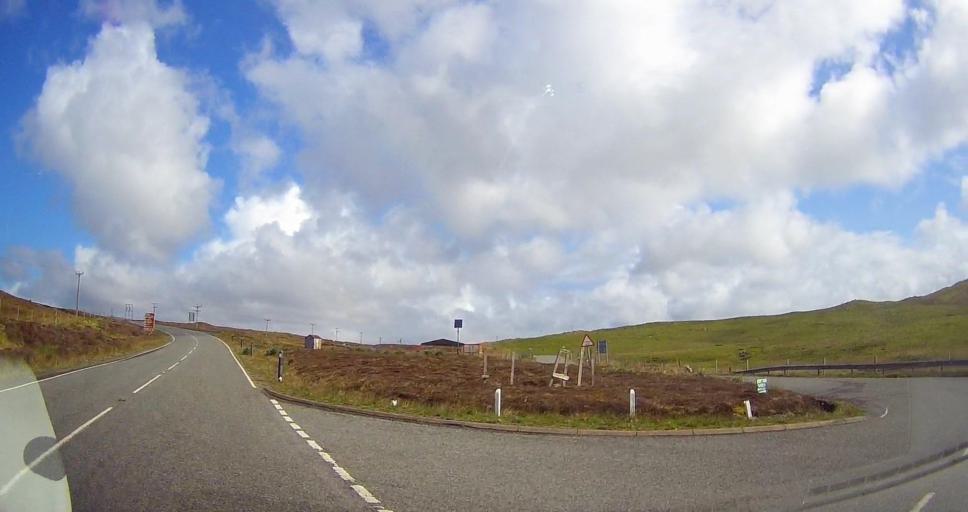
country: GB
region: Scotland
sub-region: Shetland Islands
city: Lerwick
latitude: 60.4759
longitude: -1.4084
